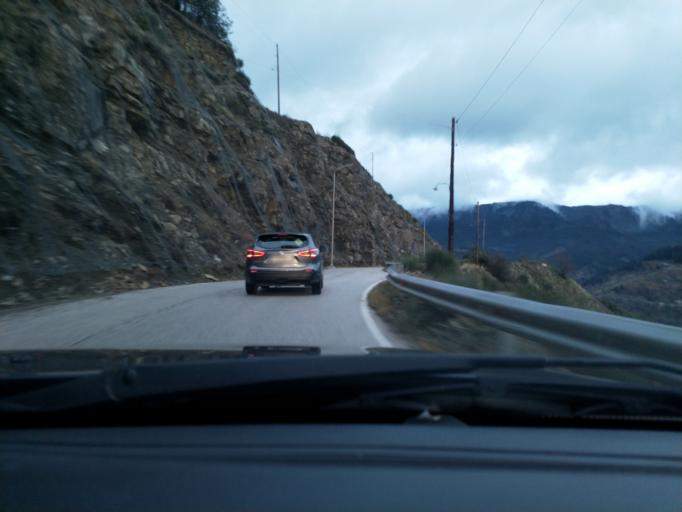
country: GR
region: Epirus
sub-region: Nomos Ioanninon
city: Metsovo
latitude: 39.7647
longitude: 21.1767
